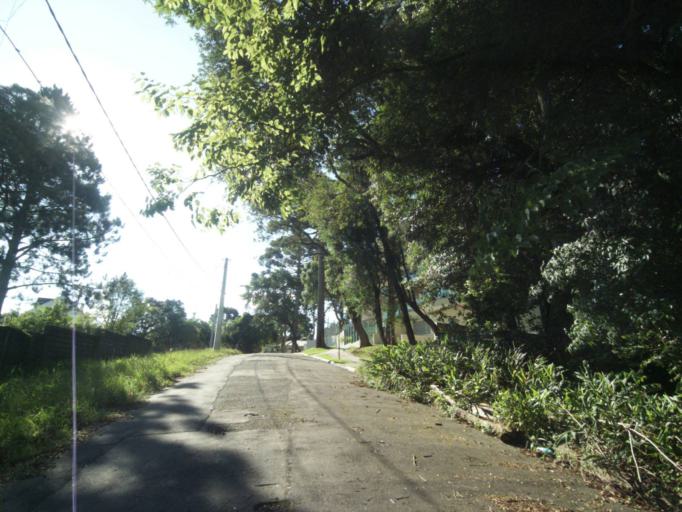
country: BR
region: Parana
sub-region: Curitiba
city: Curitiba
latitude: -25.4519
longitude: -49.3174
